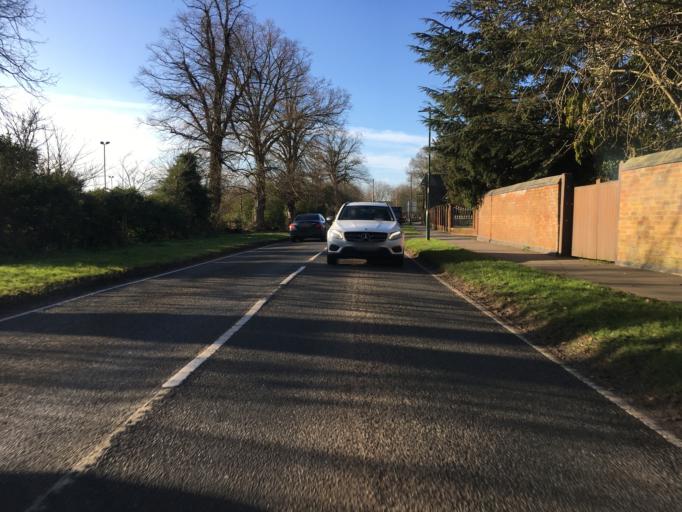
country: GB
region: England
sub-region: Warwickshire
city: Stratford-upon-Avon
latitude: 52.2027
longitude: -1.6686
